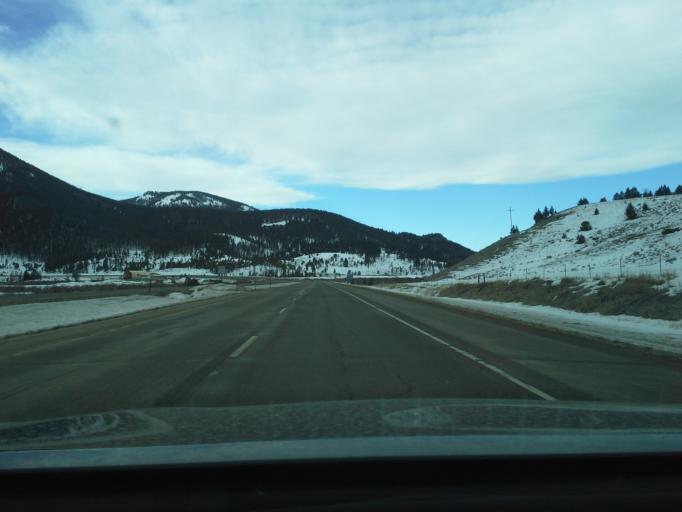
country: US
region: Montana
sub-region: Jefferson County
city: Boulder
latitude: 46.2630
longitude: -112.3304
